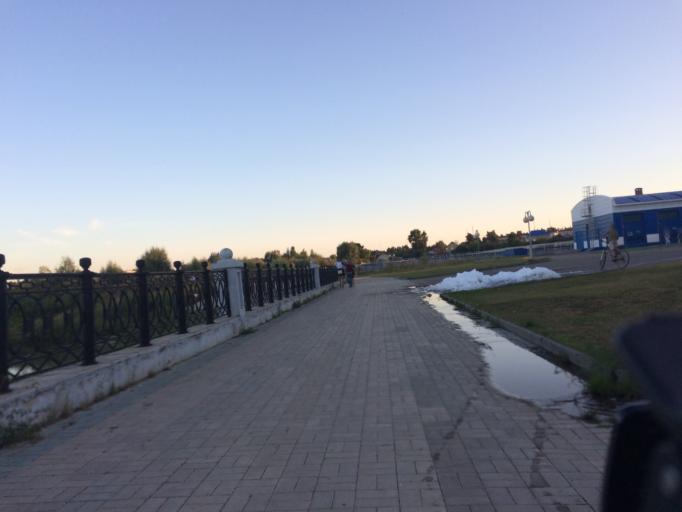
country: RU
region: Mariy-El
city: Yoshkar-Ola
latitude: 56.6244
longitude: 47.8962
